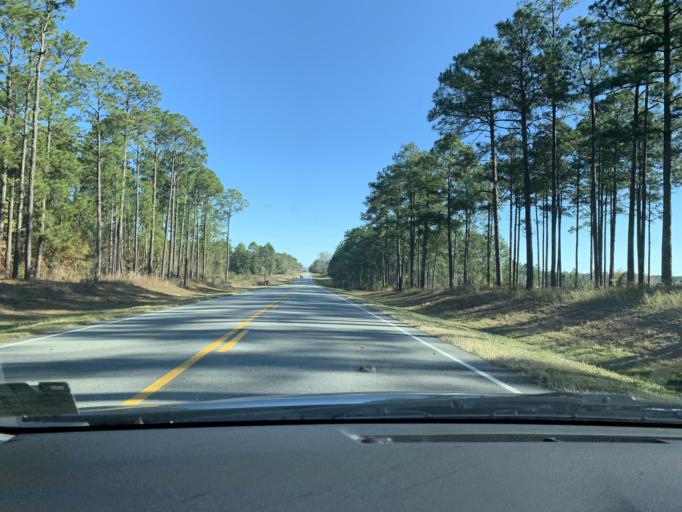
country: US
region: Georgia
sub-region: Ben Hill County
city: Fitzgerald
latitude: 31.7330
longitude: -83.1694
